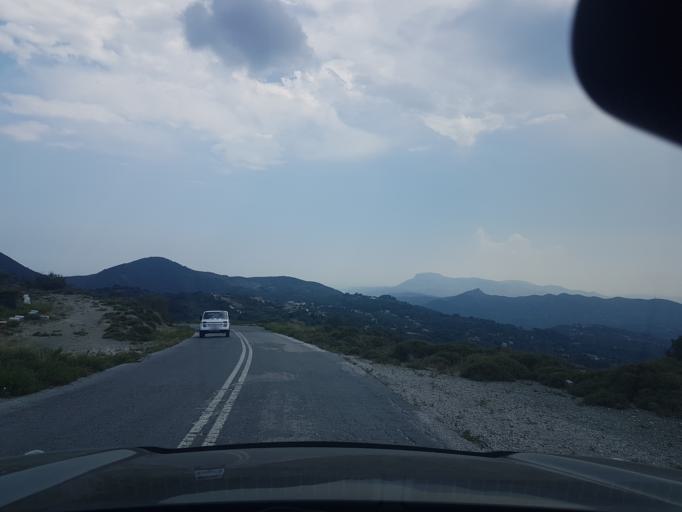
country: GR
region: Central Greece
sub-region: Nomos Evvoias
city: Kymi
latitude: 38.6443
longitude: 24.0589
